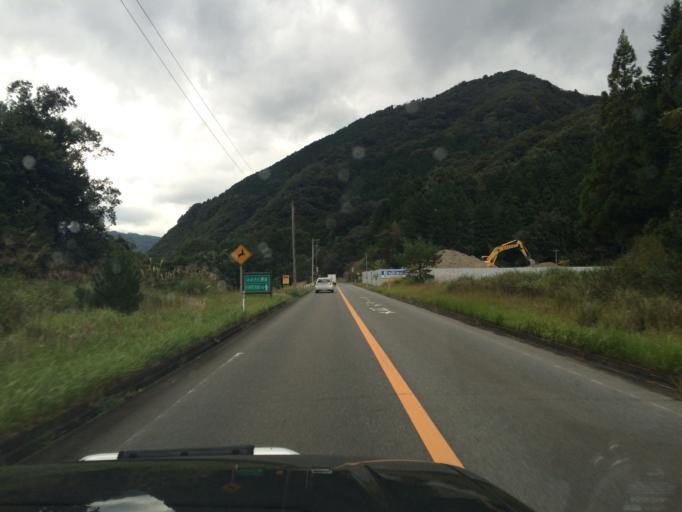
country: JP
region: Hyogo
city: Toyooka
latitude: 35.4408
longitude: 134.7939
